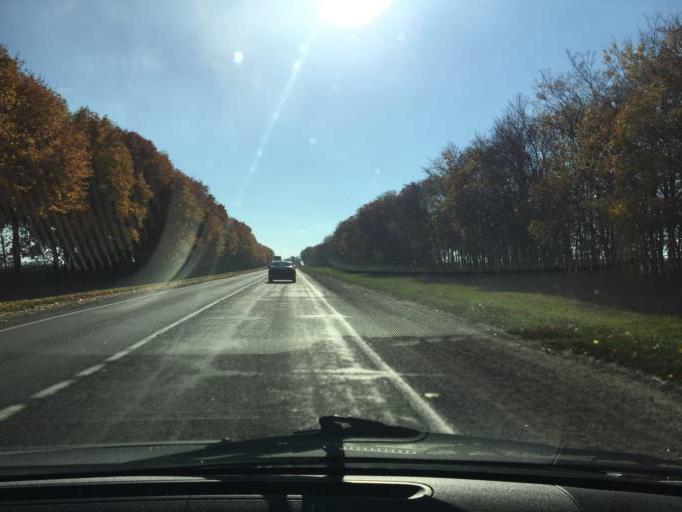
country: BY
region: Minsk
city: Salihorsk
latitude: 52.8843
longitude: 27.4697
